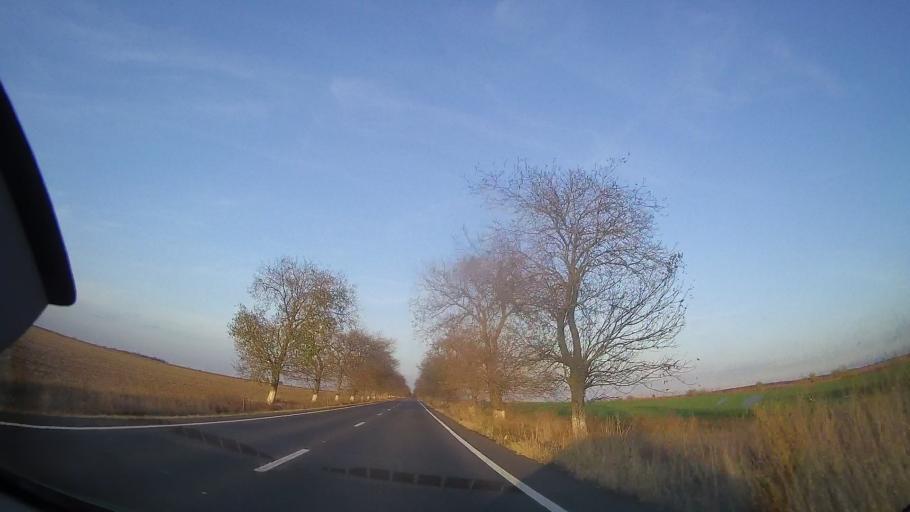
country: RO
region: Constanta
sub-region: Comuna Amzacea
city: Amzacea
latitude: 43.9481
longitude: 28.3793
